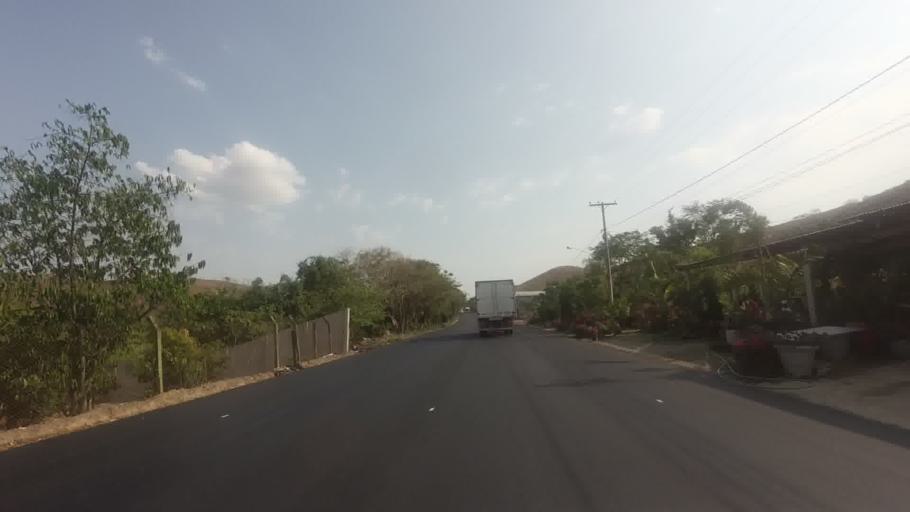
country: BR
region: Rio de Janeiro
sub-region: Bom Jesus Do Itabapoana
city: Bom Jesus do Itabapoana
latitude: -21.1454
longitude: -41.6654
